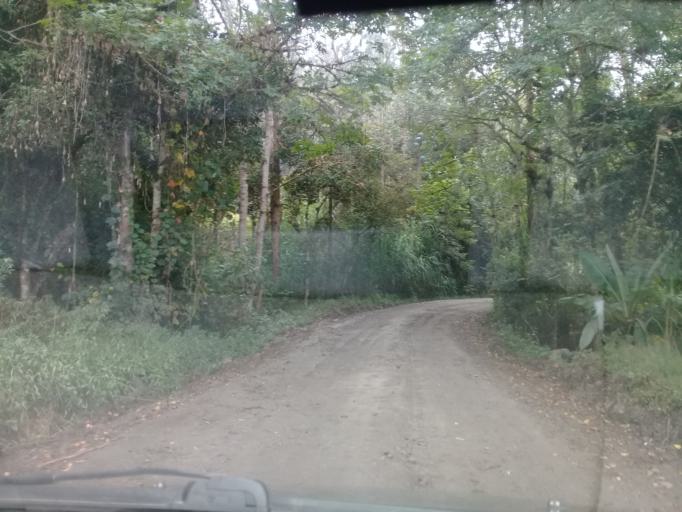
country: CO
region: Cundinamarca
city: Caqueza
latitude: 4.3916
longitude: -73.9787
